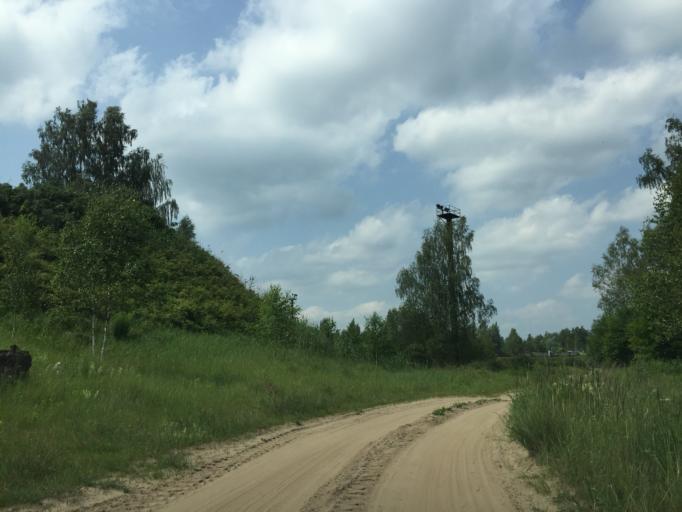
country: LV
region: Olaine
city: Olaine
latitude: 56.7719
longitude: 23.9137
